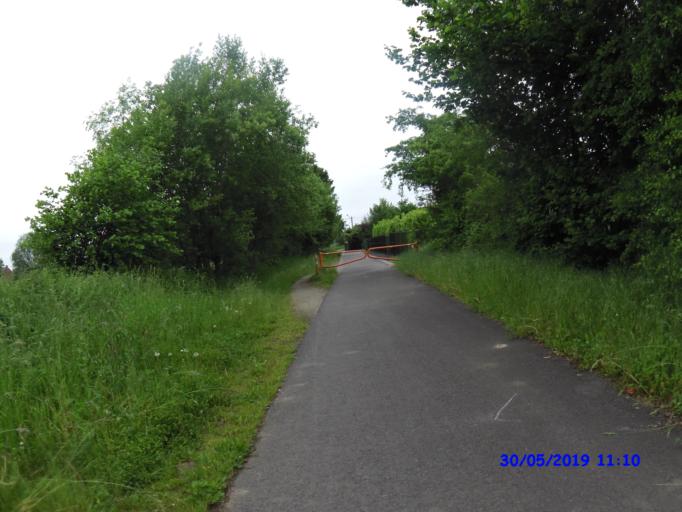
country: BE
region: Wallonia
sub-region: Province du Hainaut
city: Thuin
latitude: 50.2954
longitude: 4.3351
